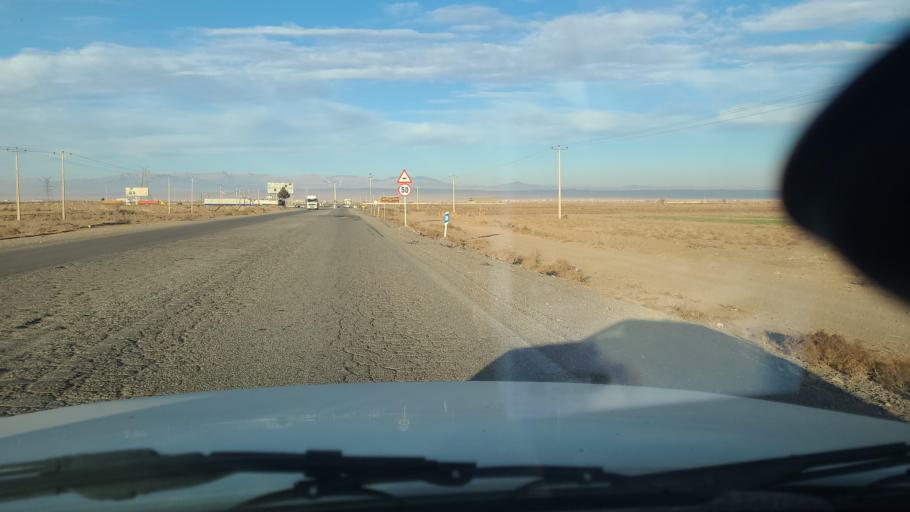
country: IR
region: Razavi Khorasan
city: Neqab
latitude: 36.5821
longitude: 57.5801
